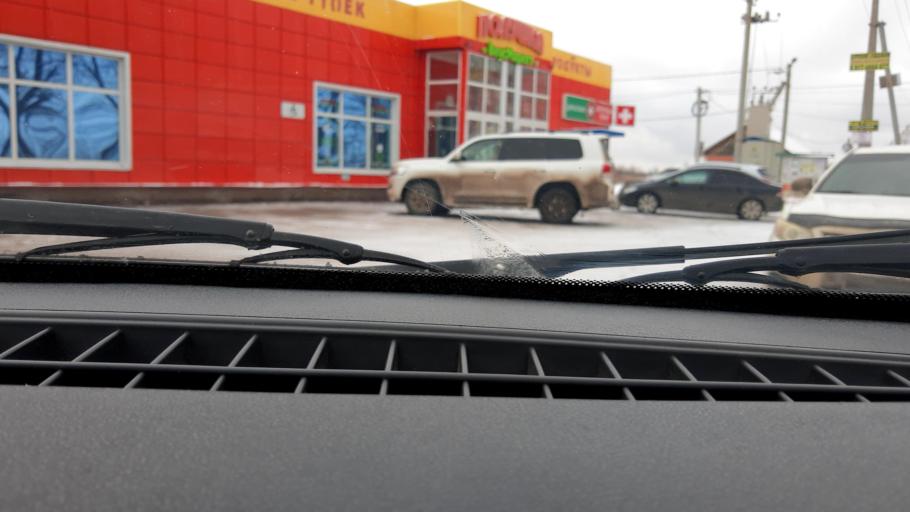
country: RU
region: Bashkortostan
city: Iglino
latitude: 54.7920
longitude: 56.2663
